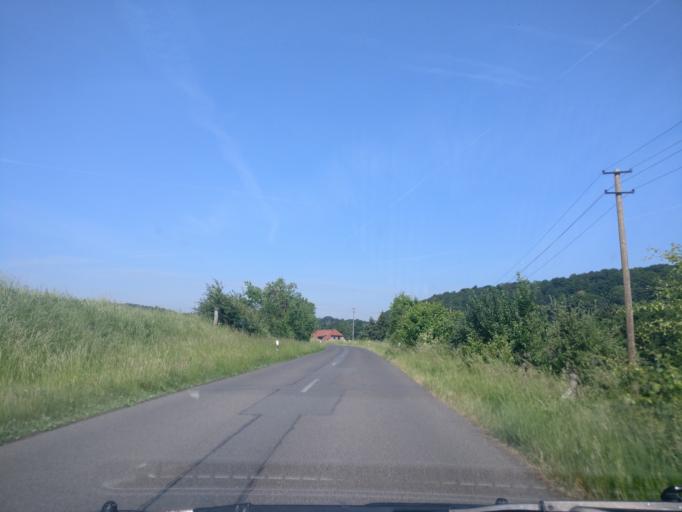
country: DE
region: Lower Saxony
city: Scheden
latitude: 51.3898
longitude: 9.7406
